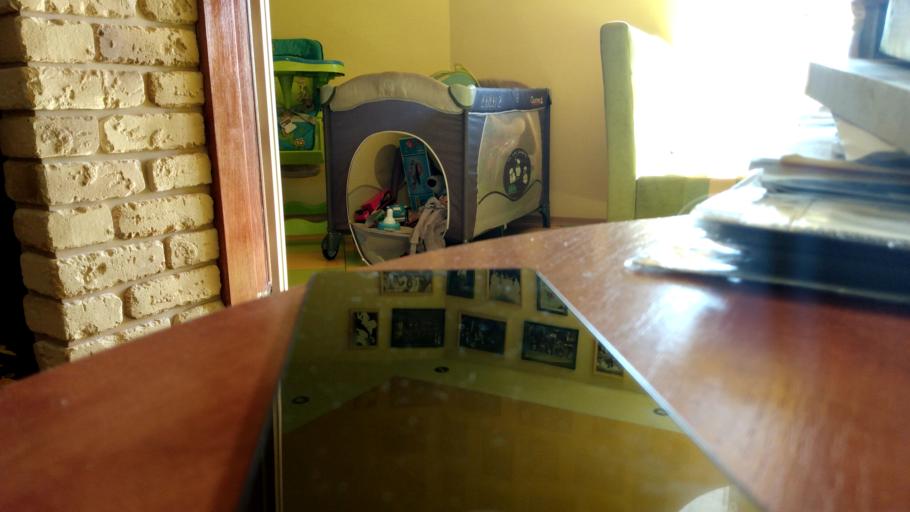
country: RU
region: Penza
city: Serdobsk
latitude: 52.2983
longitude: 44.3993
